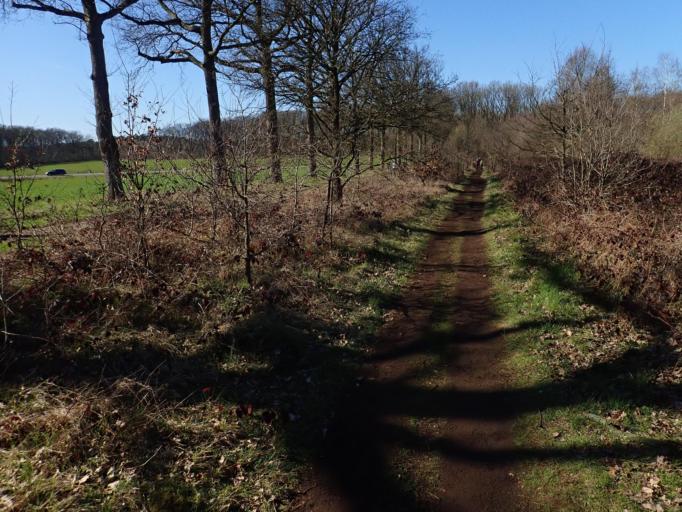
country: BE
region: Flanders
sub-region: Provincie Vlaams-Brabant
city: Scherpenheuvel-Zichem
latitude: 51.0375
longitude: 4.9851
